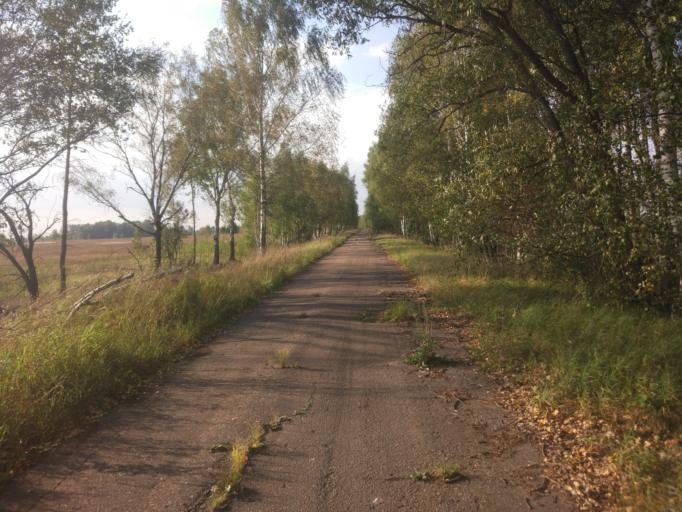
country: RU
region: Brjansk
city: Vyshkov
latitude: 52.6593
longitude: 31.5788
